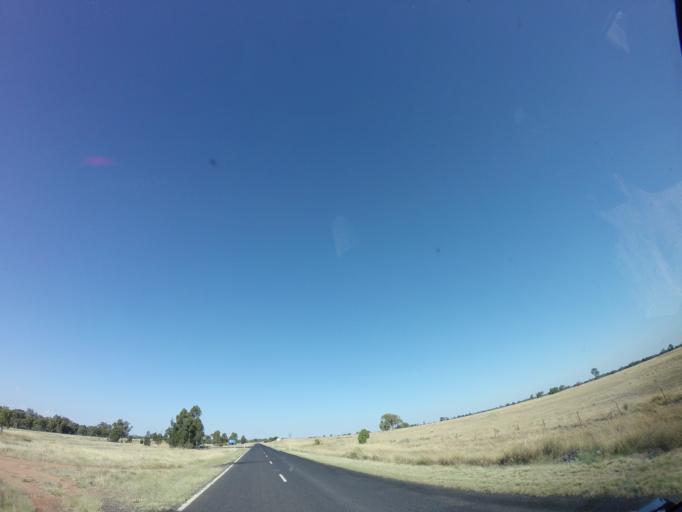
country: AU
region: New South Wales
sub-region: Gilgandra
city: Gilgandra
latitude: -31.6585
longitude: 148.4457
